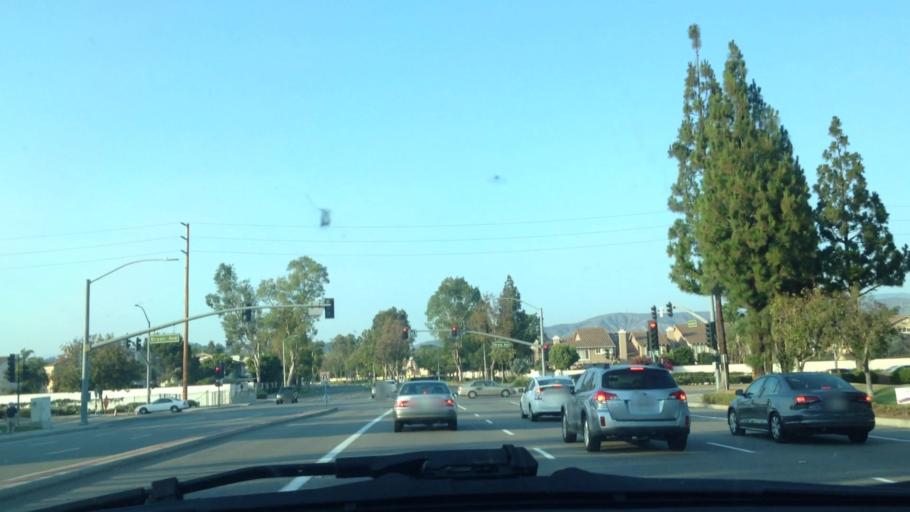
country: US
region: California
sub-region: Orange County
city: Tustin
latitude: 33.7305
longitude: -117.7990
